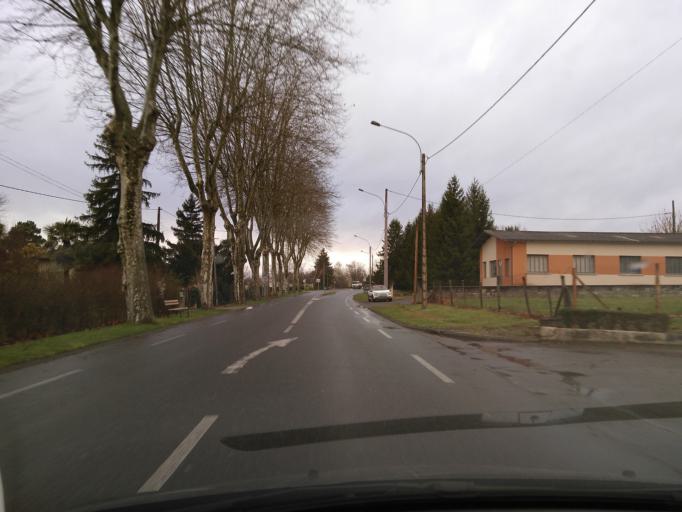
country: FR
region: Midi-Pyrenees
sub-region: Departement de la Haute-Garonne
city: Montesquieu-Volvestre
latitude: 43.2140
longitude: 1.2238
